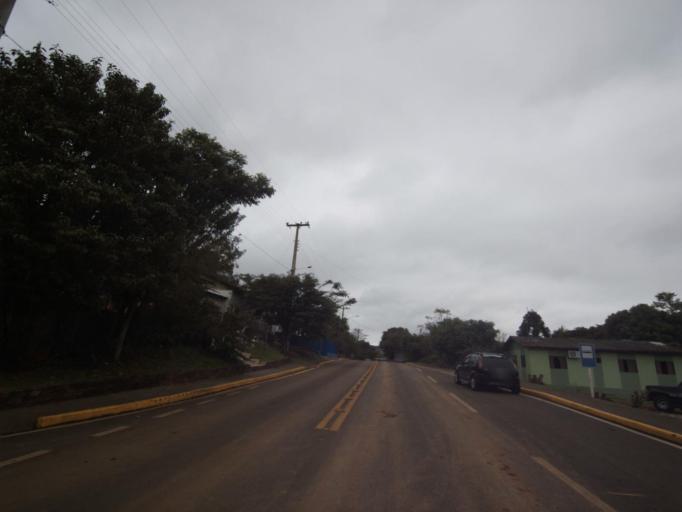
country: AR
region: Misiones
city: El Soberbio
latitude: -27.2952
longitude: -54.1901
